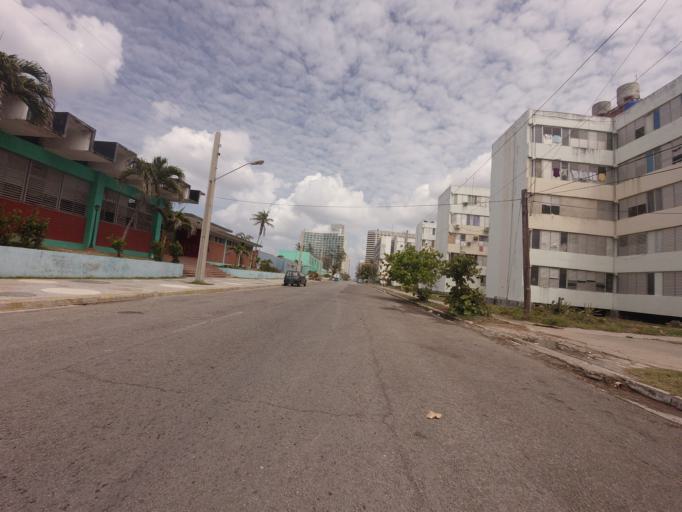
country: CU
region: La Habana
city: Havana
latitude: 23.1373
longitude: -82.4067
